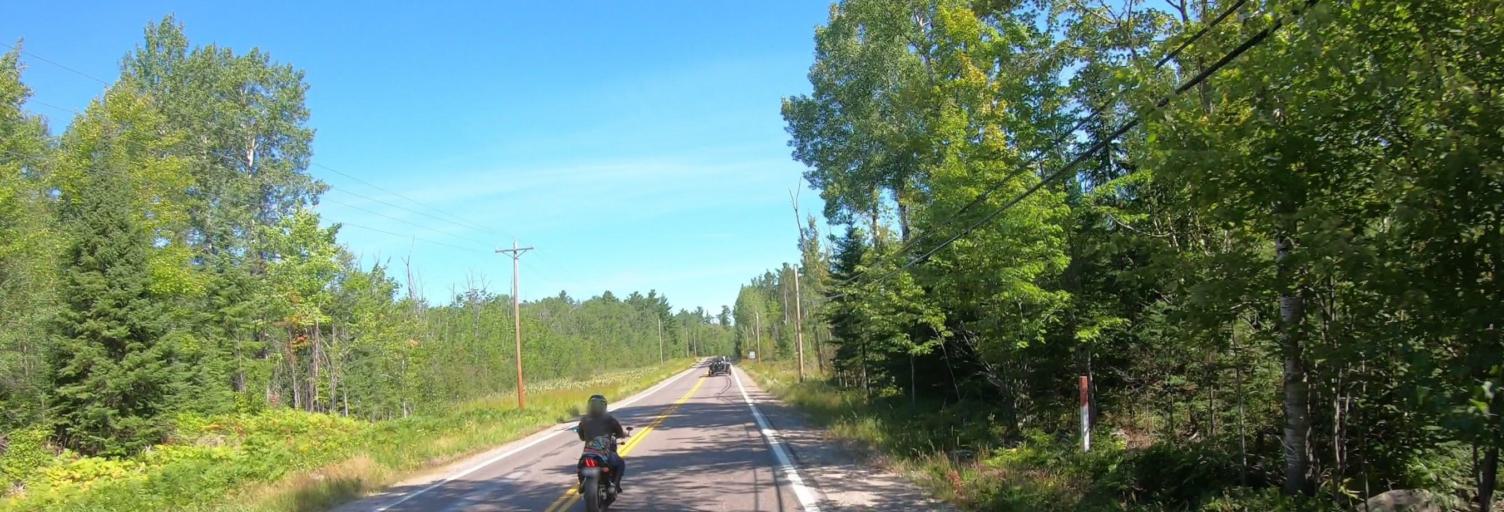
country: US
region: Minnesota
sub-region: Saint Louis County
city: Mountain Iron
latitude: 47.9350
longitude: -92.6766
